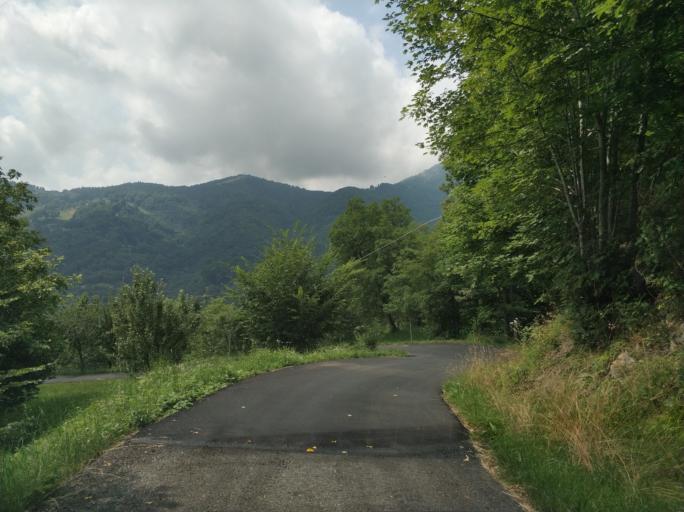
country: IT
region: Piedmont
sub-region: Provincia di Torino
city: Viu
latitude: 45.1999
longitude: 7.3810
